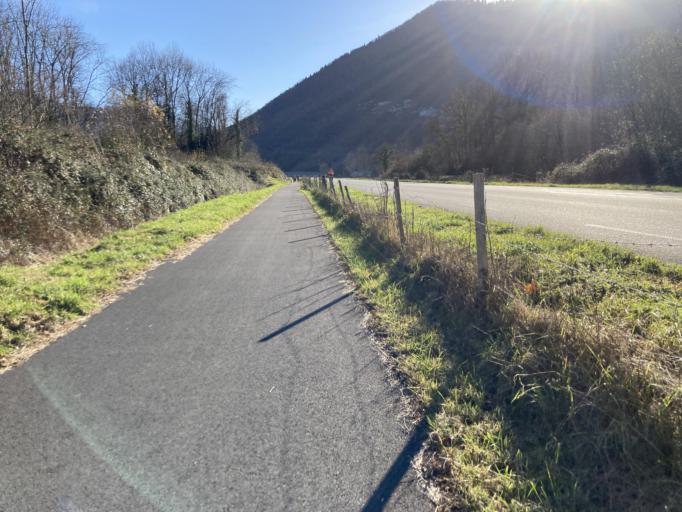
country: FR
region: Aquitaine
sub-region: Departement des Pyrenees-Atlantiques
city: Louvie-Juzon
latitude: 43.0980
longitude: -0.4329
